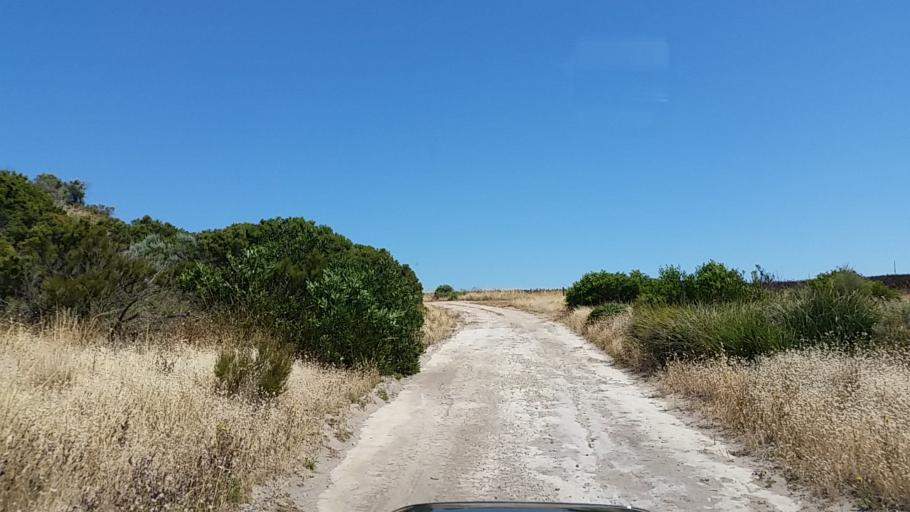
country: AU
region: South Australia
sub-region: Yorke Peninsula
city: Honiton
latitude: -35.2358
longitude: 137.1166
